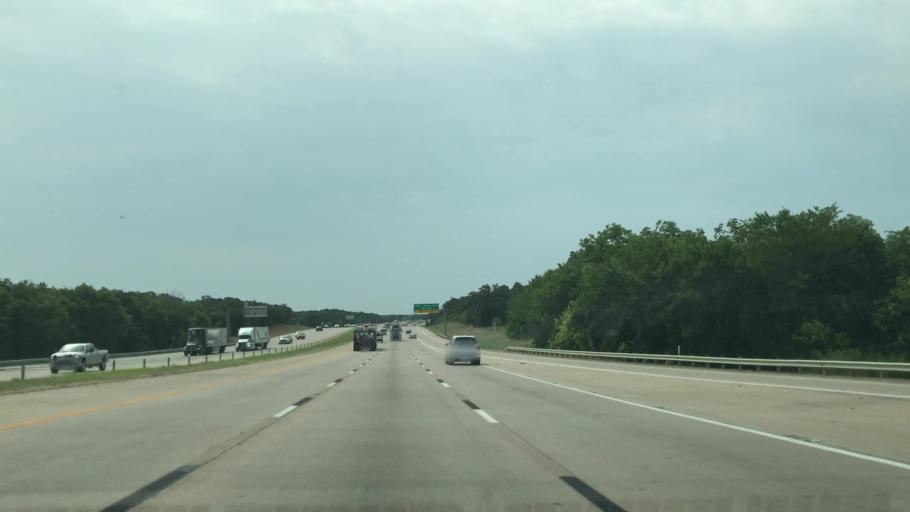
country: US
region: Texas
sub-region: Denton County
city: Trophy Club
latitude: 32.9803
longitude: -97.1659
